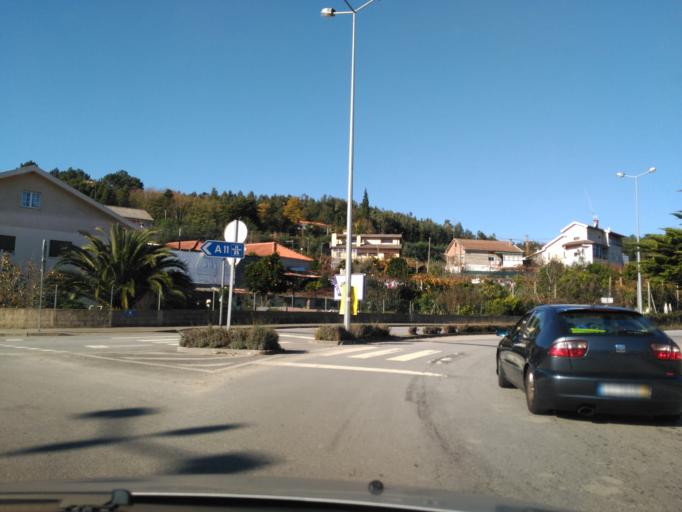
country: PT
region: Braga
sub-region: Braga
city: Adaufe
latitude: 41.5737
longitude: -8.3686
